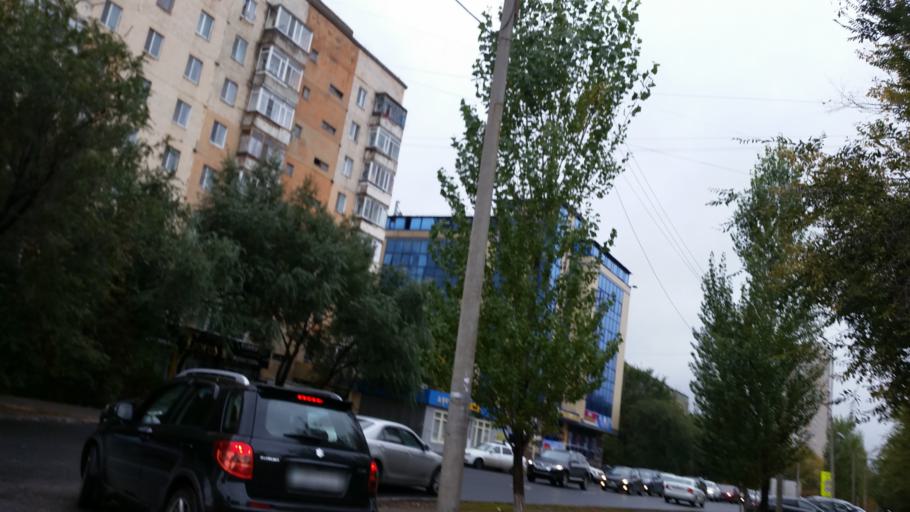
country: KZ
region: Astana Qalasy
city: Astana
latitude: 51.1491
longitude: 71.4687
